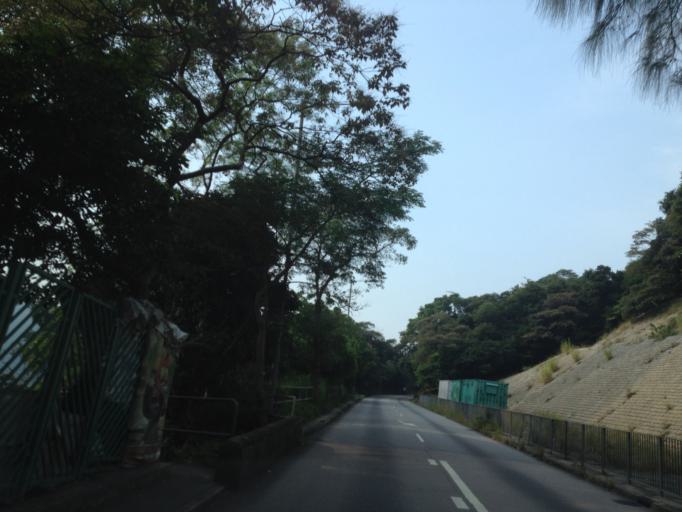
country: HK
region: Wanchai
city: Wan Chai
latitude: 22.2664
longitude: 114.2320
